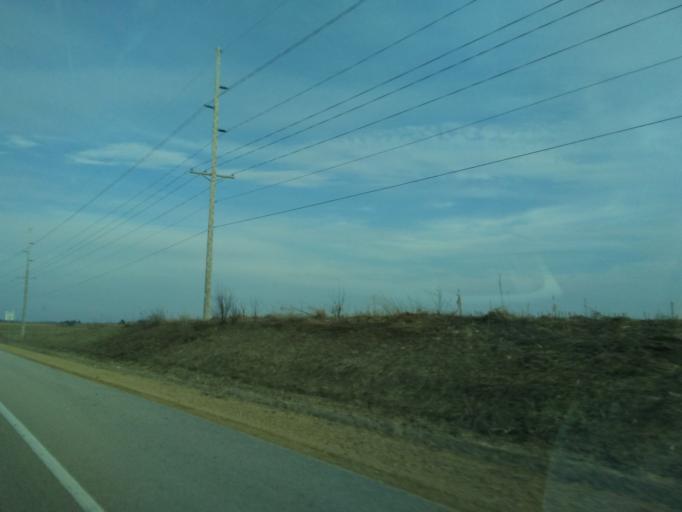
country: US
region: Wisconsin
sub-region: Iowa County
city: Dodgeville
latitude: 42.9677
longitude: -90.2456
